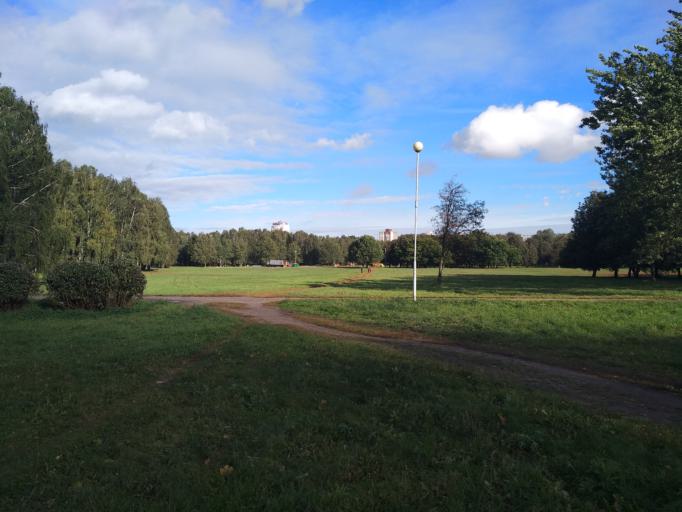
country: BY
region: Minsk
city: Minsk
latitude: 53.9301
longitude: 27.5671
